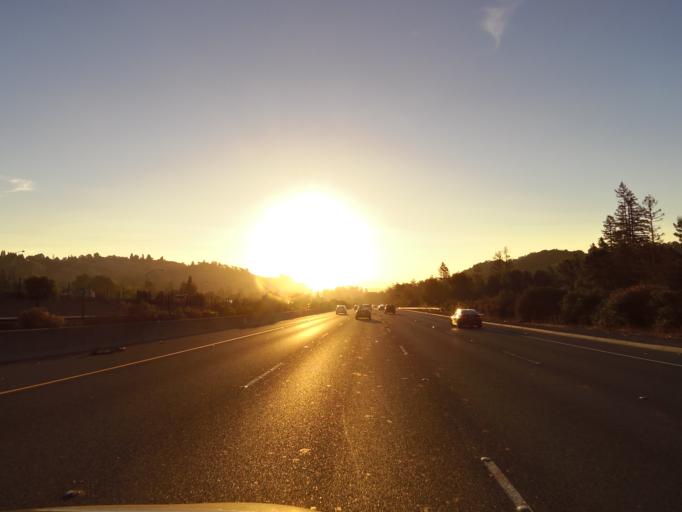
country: US
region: California
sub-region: Contra Costa County
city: Orinda
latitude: 37.8922
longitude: -122.1568
